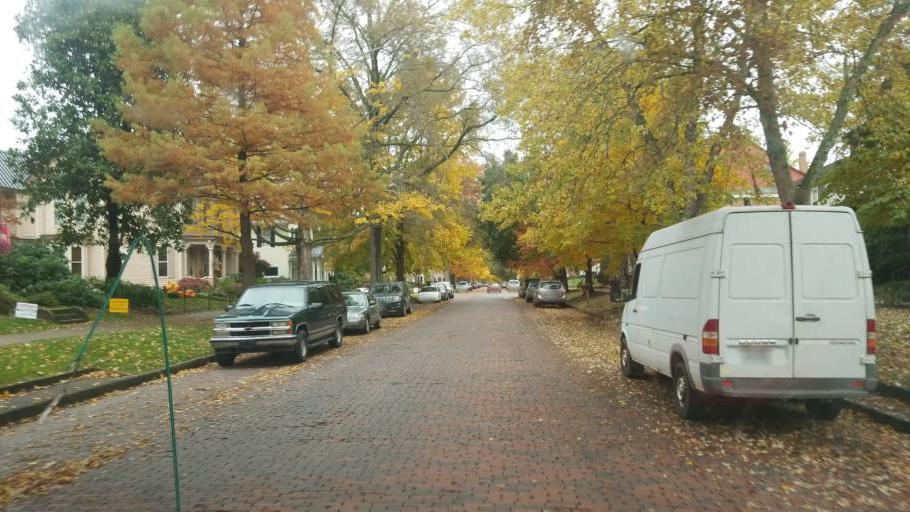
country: US
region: Ohio
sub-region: Washington County
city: Marietta
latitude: 39.4210
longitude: -81.4540
